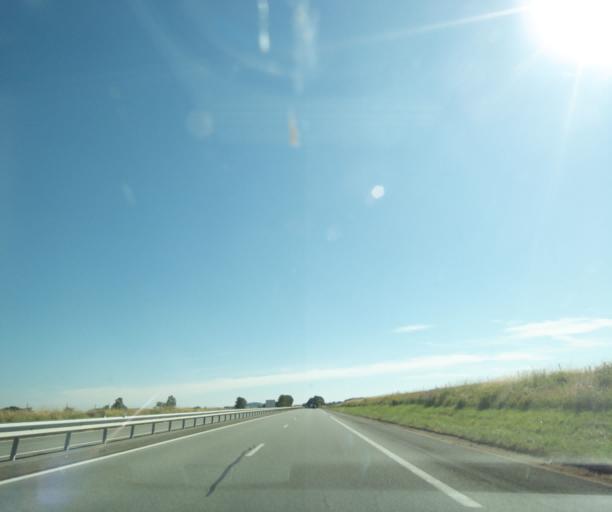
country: FR
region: Champagne-Ardenne
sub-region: Departement de la Haute-Marne
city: Avrecourt
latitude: 48.0224
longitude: 5.5346
